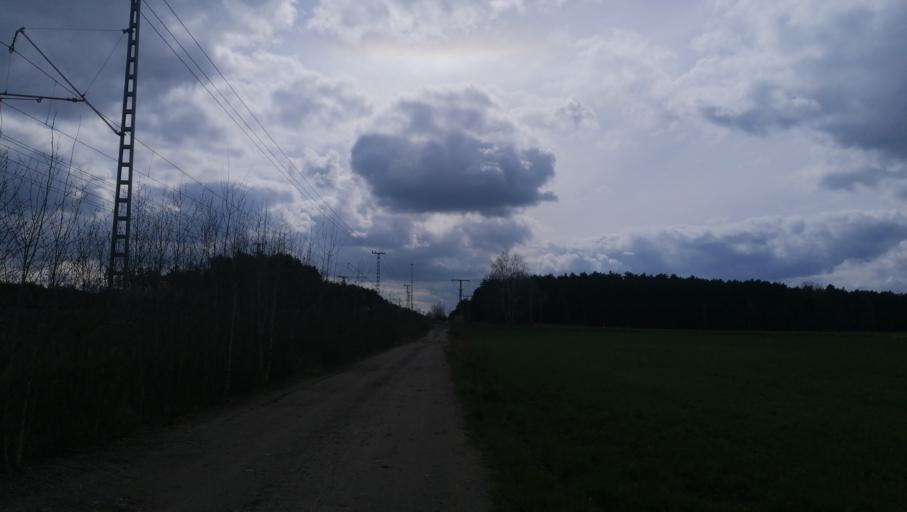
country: DE
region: Brandenburg
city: Cottbus
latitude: 51.6843
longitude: 14.3362
